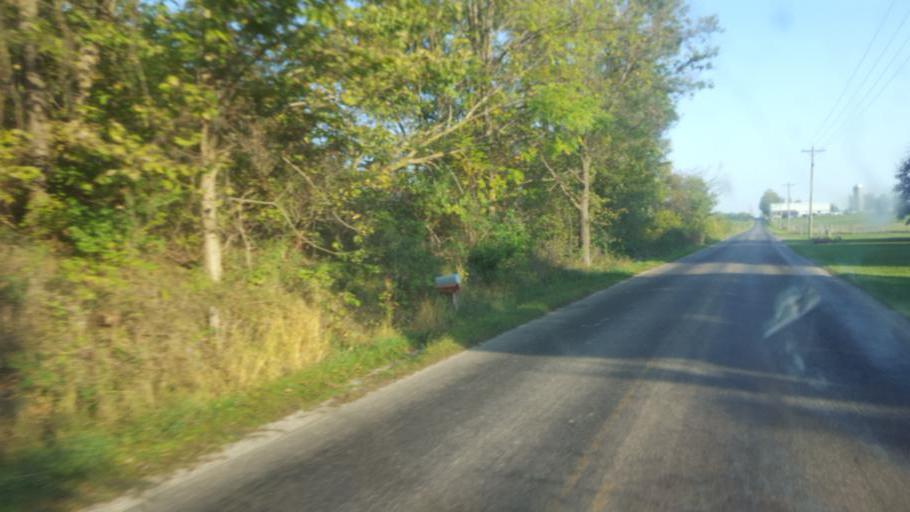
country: US
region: Indiana
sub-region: LaGrange County
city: Lagrange
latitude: 41.5929
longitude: -85.4241
